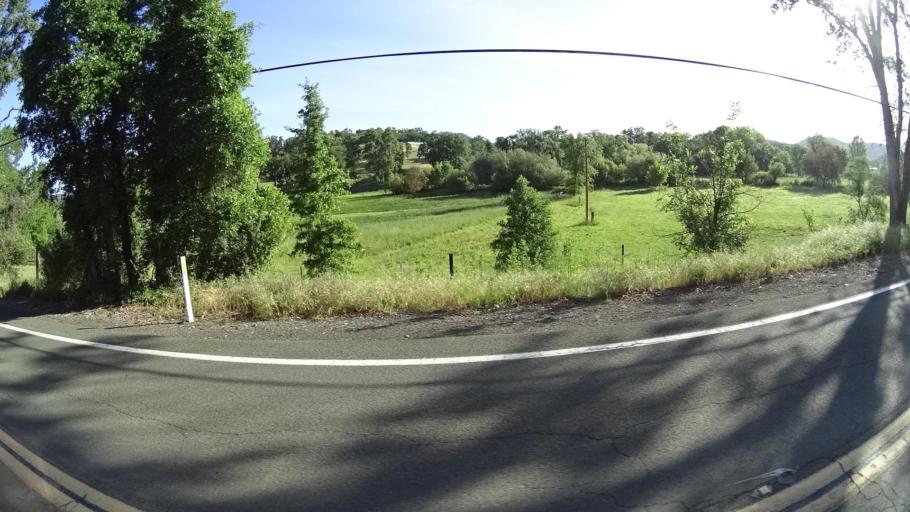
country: US
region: California
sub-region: Lake County
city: North Lakeport
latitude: 39.0952
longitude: -122.9673
